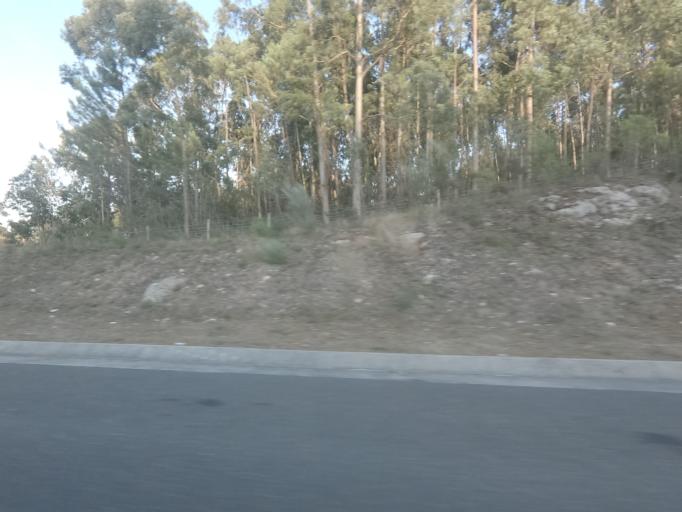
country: PT
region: Leiria
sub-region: Leiria
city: Santa Catarina da Serra
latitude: 39.6603
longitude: -8.6931
